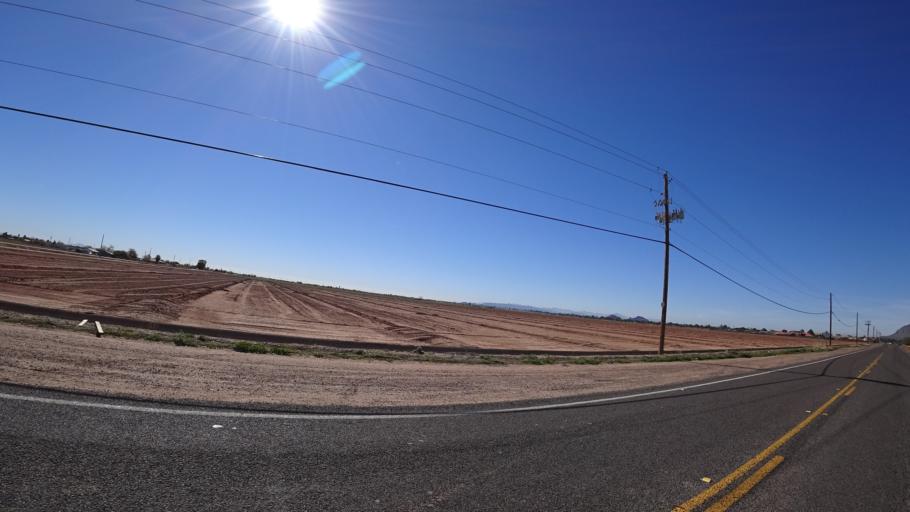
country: US
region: Arizona
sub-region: Maricopa County
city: Scottsdale
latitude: 33.5095
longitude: -111.8748
